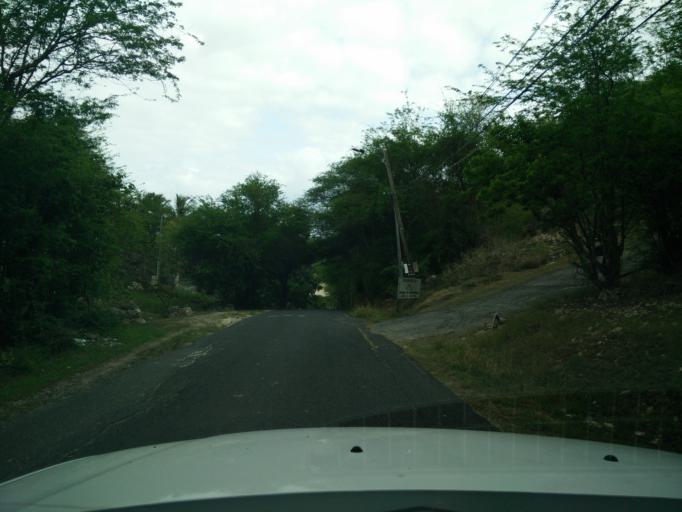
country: GP
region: Guadeloupe
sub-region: Guadeloupe
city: Le Gosier
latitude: 16.2322
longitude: -61.4422
